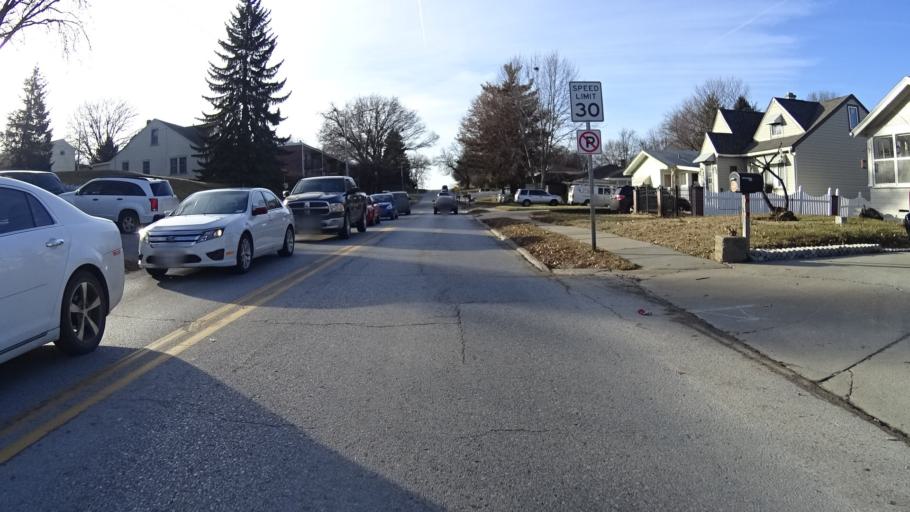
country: US
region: Nebraska
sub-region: Sarpy County
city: La Vista
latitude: 41.1909
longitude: -95.9679
